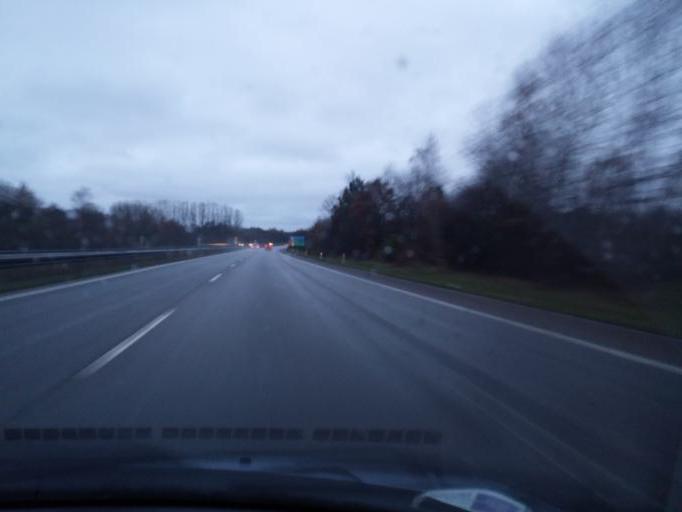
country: DK
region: South Denmark
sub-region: Odense Kommune
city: Odense
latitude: 55.3545
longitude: 10.3679
